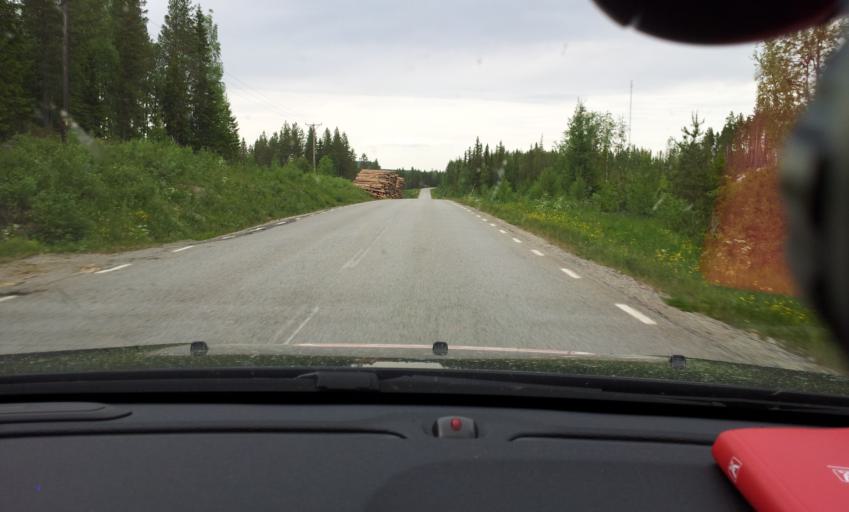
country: SE
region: Jaemtland
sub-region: Bergs Kommun
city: Hoverberg
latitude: 62.6964
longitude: 14.6258
